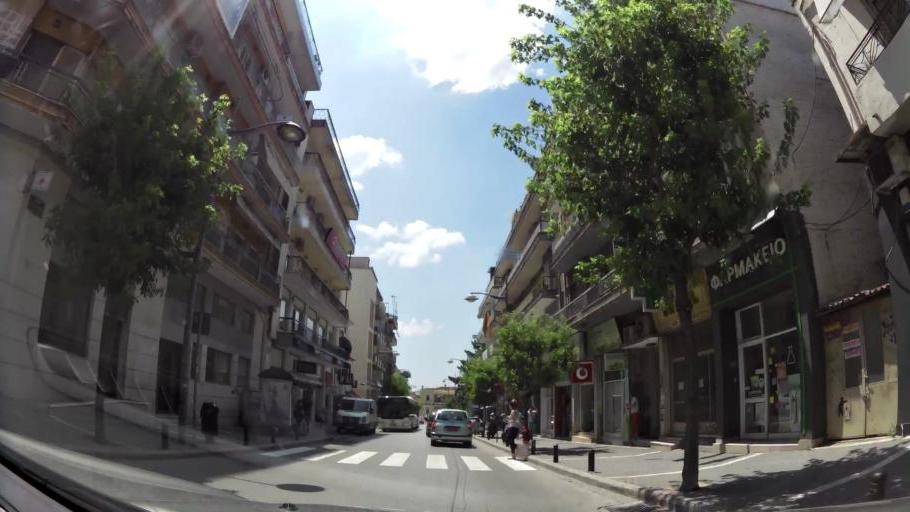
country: GR
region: West Macedonia
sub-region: Nomos Kozanis
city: Kozani
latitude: 40.3024
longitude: 21.7883
